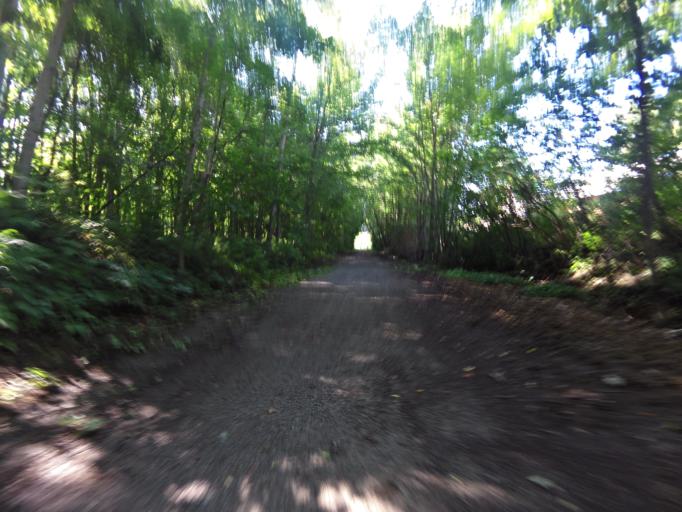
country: CA
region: Ontario
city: Ottawa
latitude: 45.2524
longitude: -75.6216
